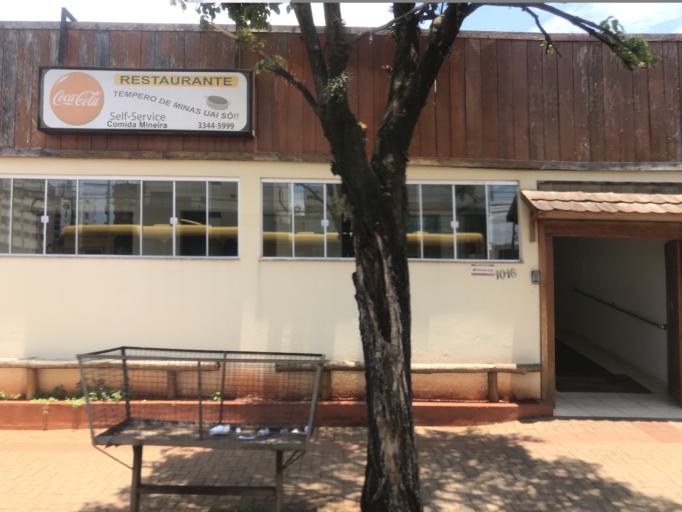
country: BR
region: Parana
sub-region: Londrina
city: Londrina
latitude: -23.3271
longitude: -51.1568
